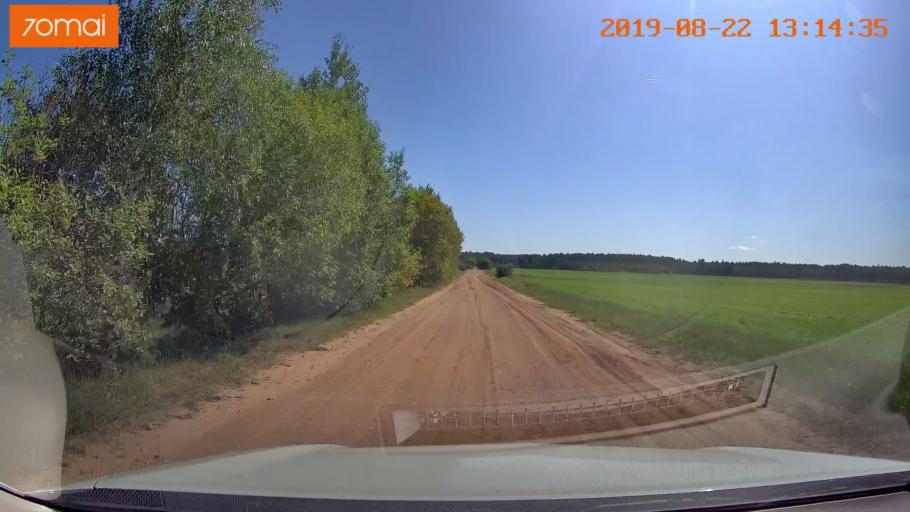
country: BY
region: Minsk
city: Prawdzinski
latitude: 53.2666
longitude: 27.8889
